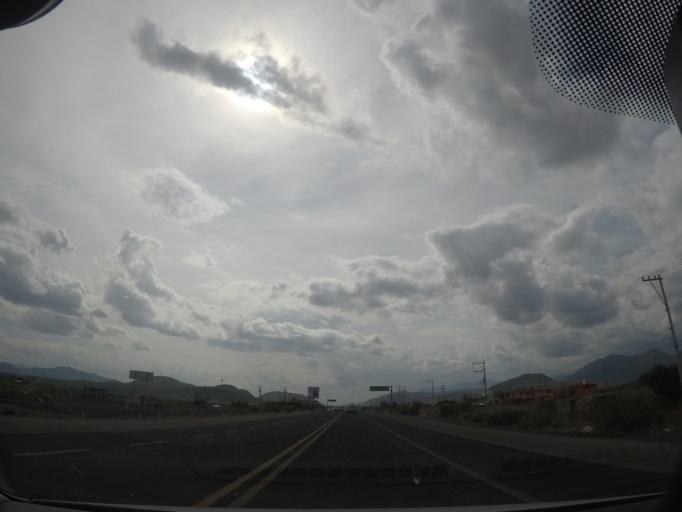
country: MX
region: Oaxaca
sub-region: San Jeronimo Tlacochahuaya
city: Macuilxochitl de Artigas Carranza
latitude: 16.9867
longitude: -96.5132
